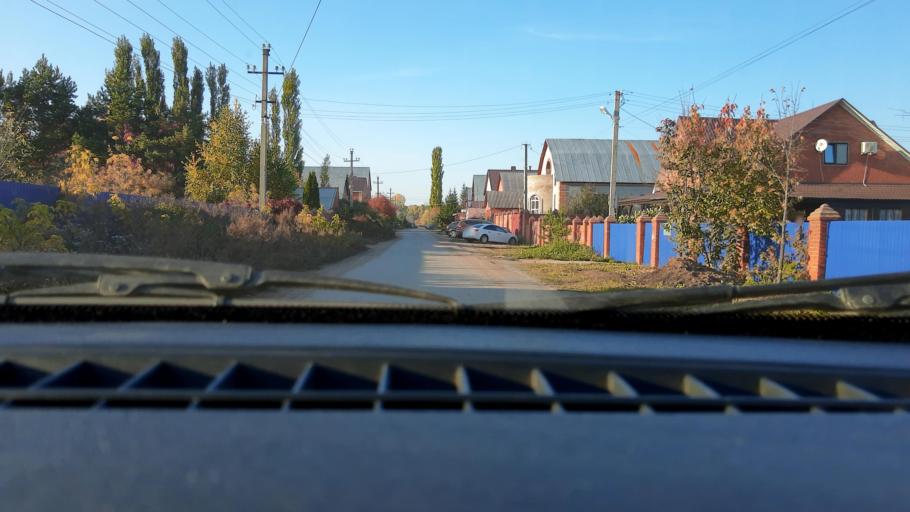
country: RU
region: Bashkortostan
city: Mikhaylovka
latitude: 54.7893
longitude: 55.8977
